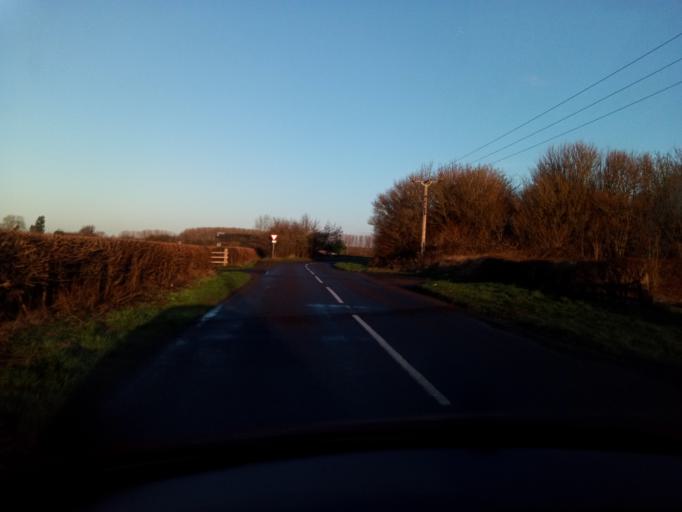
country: GB
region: England
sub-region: Leicestershire
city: Loughborough
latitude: 52.7788
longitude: -1.1730
